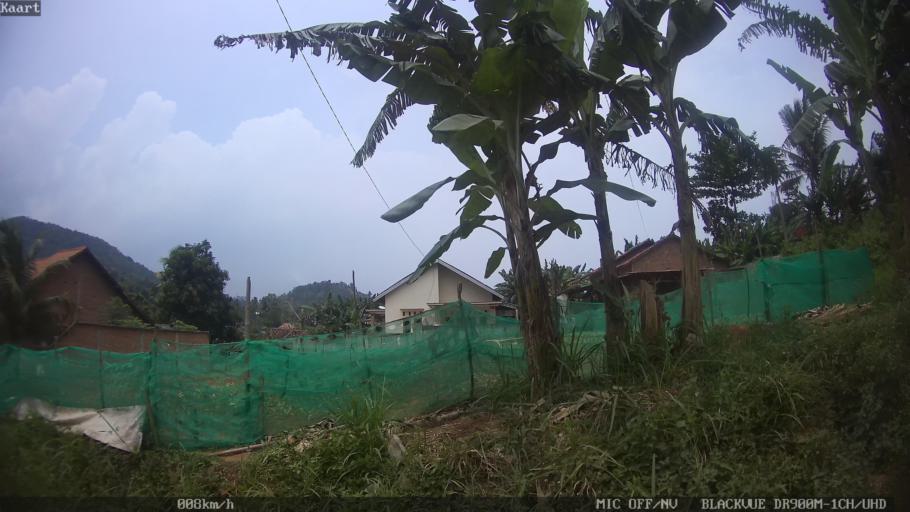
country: ID
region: Lampung
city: Kedaton
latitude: -5.3972
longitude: 105.3259
